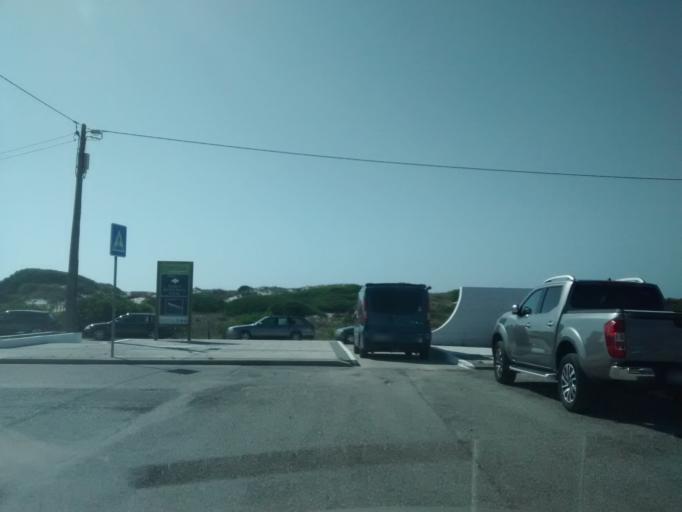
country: PT
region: Aveiro
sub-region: Ilhavo
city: Gafanha da Nazare
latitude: 40.6688
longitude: -8.7428
